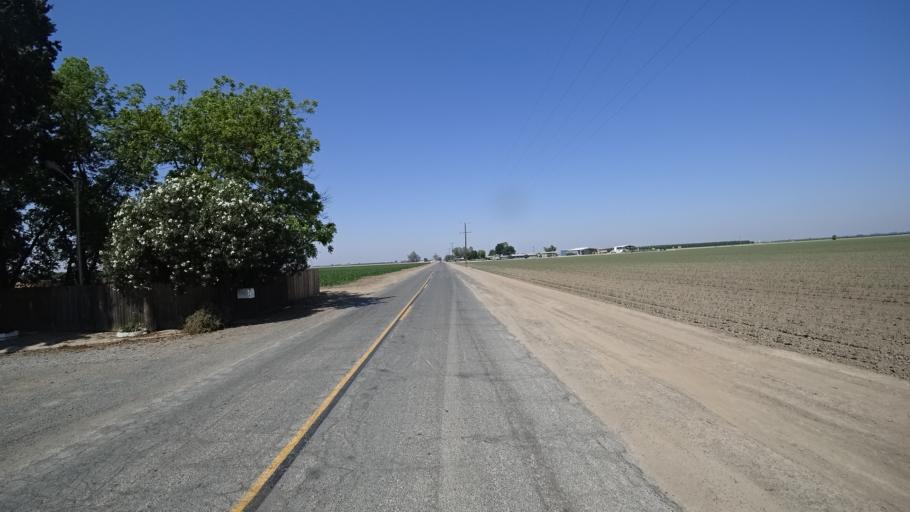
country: US
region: California
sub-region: Kings County
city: Hanford
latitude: 36.3721
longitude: -119.5472
